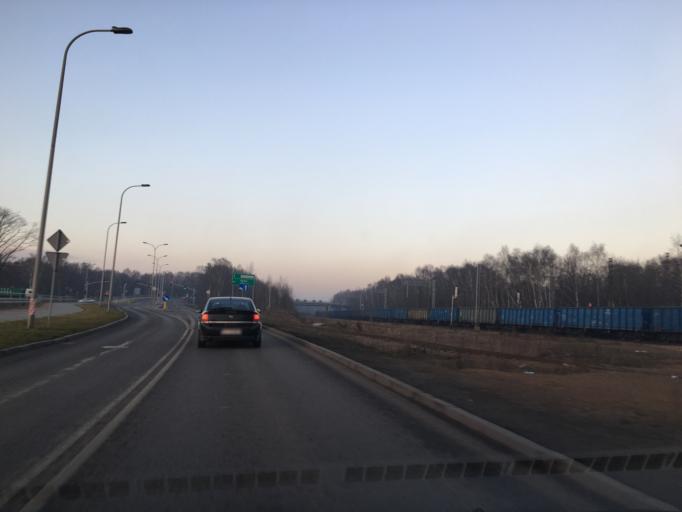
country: PL
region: Silesian Voivodeship
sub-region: Powiat tarnogorski
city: Radzionkow
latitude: 50.3668
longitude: 18.8769
